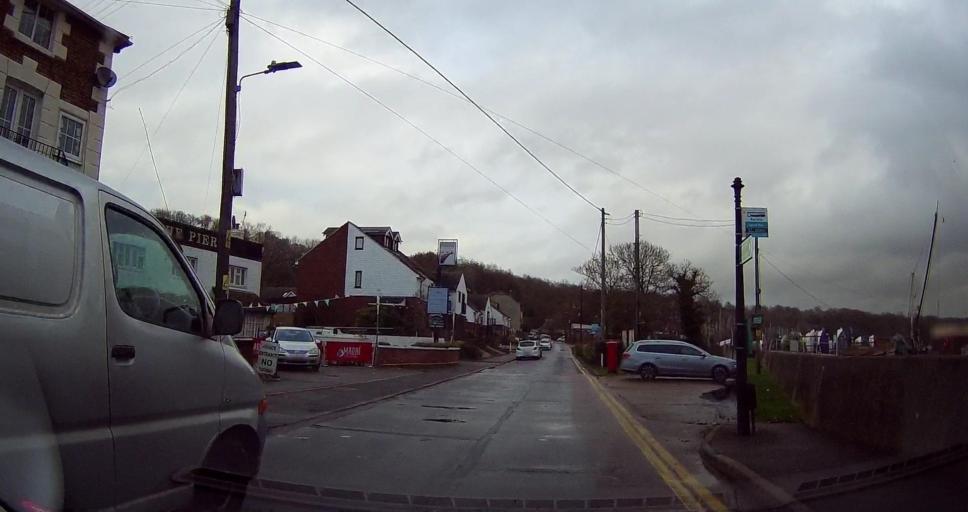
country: GB
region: England
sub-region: Kent
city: Gillingham
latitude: 51.4118
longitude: 0.5305
